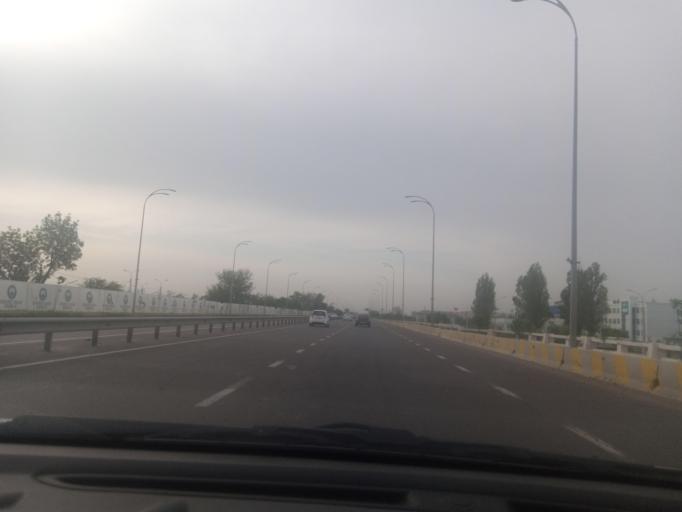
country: UZ
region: Toshkent Shahri
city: Bektemir
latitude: 41.2651
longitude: 69.3701
